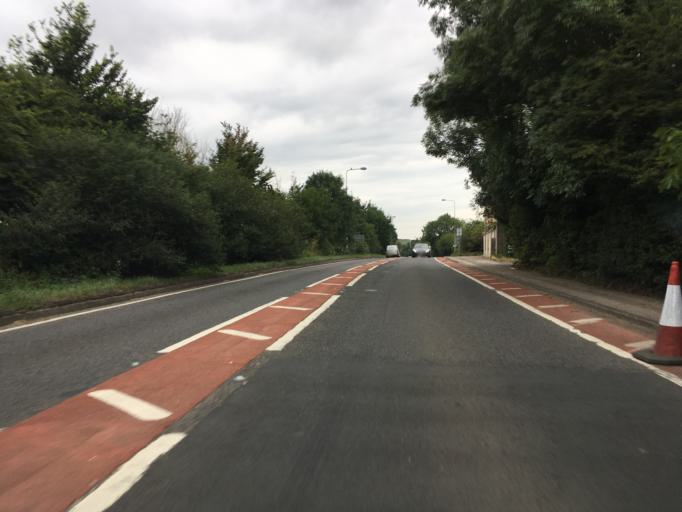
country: GB
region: England
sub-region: Central Bedfordshire
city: Hockliffe
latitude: 51.9241
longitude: -0.5759
